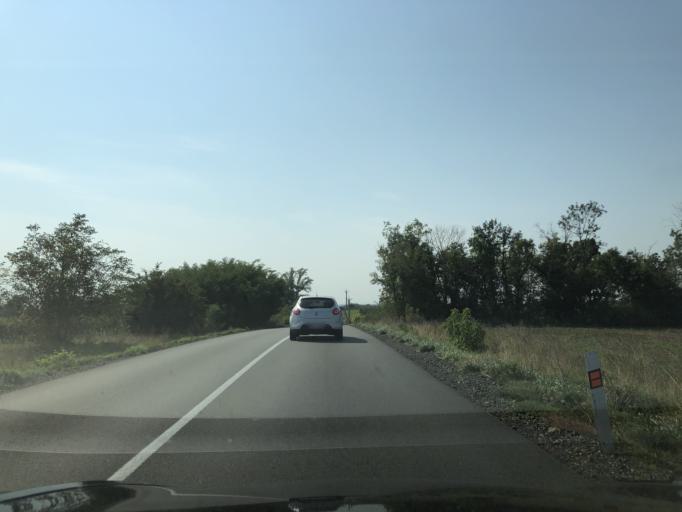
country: CZ
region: South Moravian
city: Drnholec
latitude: 48.9093
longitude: 16.5214
